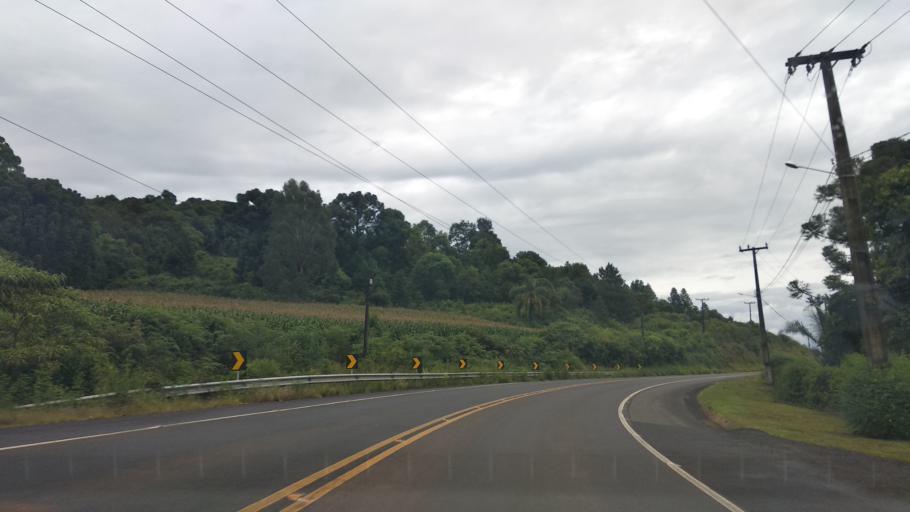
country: BR
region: Santa Catarina
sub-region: Videira
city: Videira
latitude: -27.0480
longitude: -51.1581
